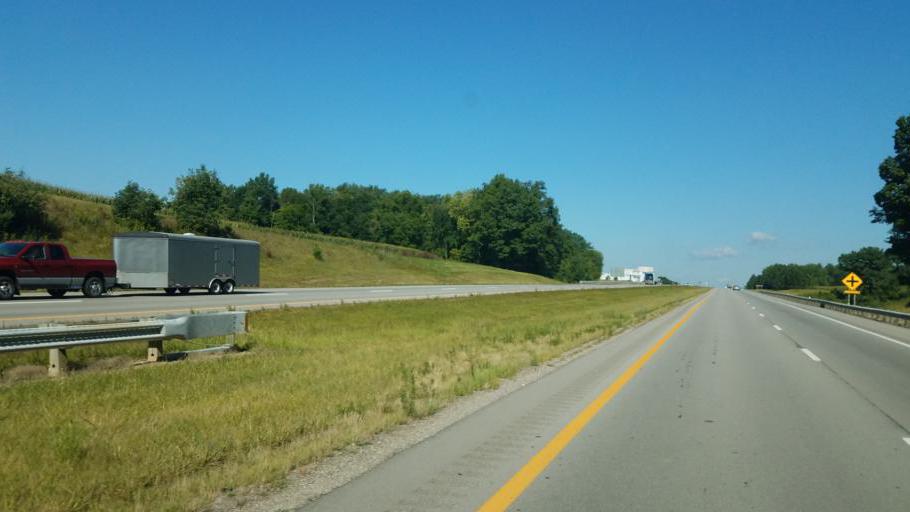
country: US
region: Ohio
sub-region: Wyandot County
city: Upper Sandusky
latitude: 40.8504
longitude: -83.2607
